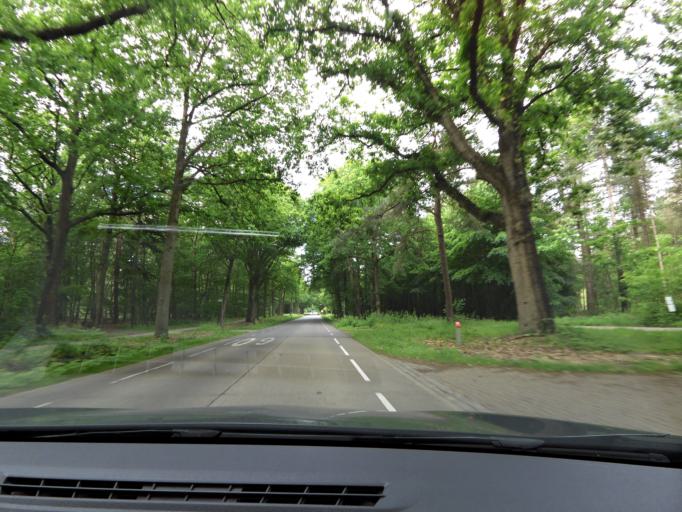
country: NL
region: North Brabant
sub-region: Gemeente Baarle-Nassau
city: Baarle-Nassau
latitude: 51.5248
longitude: 4.8883
